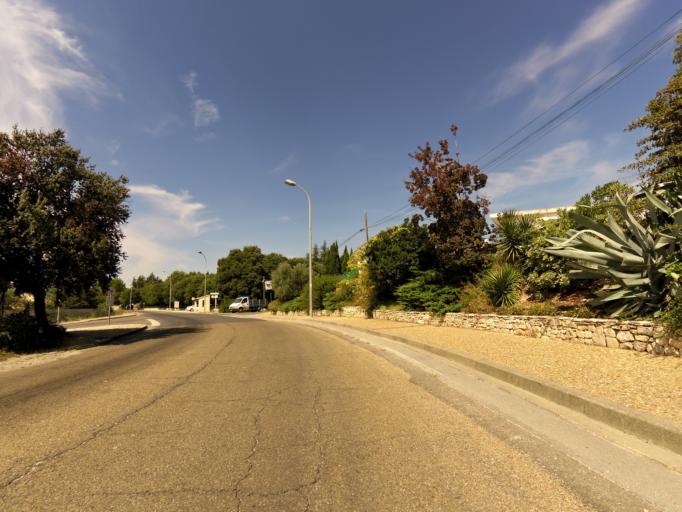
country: FR
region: Languedoc-Roussillon
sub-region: Departement du Gard
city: Vergeze
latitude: 43.7472
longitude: 4.2202
